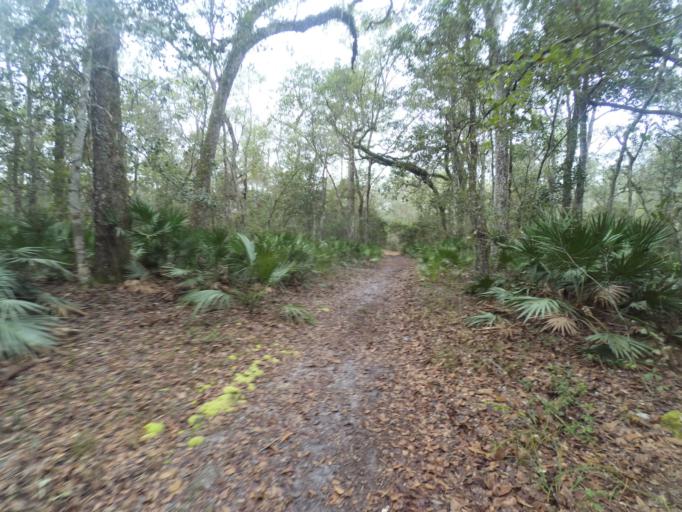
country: US
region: Florida
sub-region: Alachua County
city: Gainesville
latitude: 29.5422
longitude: -82.2769
